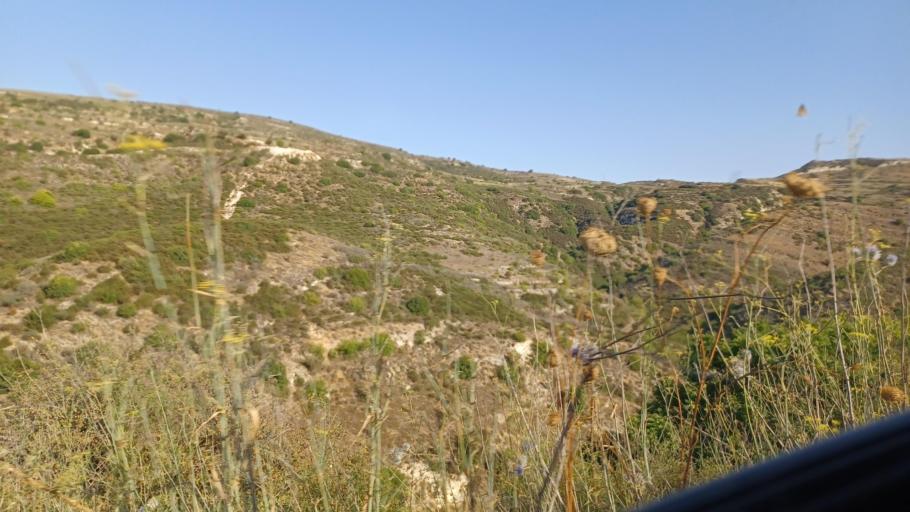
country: CY
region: Pafos
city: Tala
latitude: 34.8901
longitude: 32.4499
